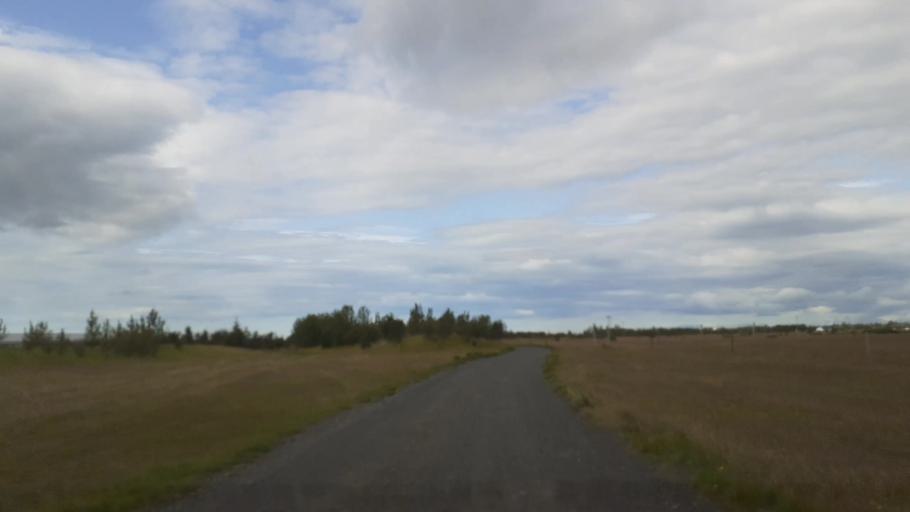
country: IS
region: South
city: Vestmannaeyjar
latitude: 63.7564
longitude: -20.2277
